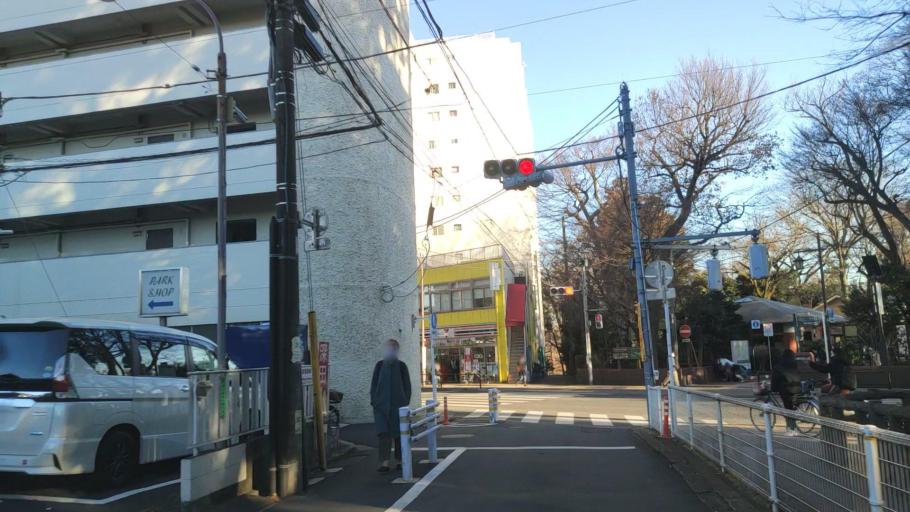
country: JP
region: Tokyo
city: Musashino
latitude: 35.7012
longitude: 139.5738
